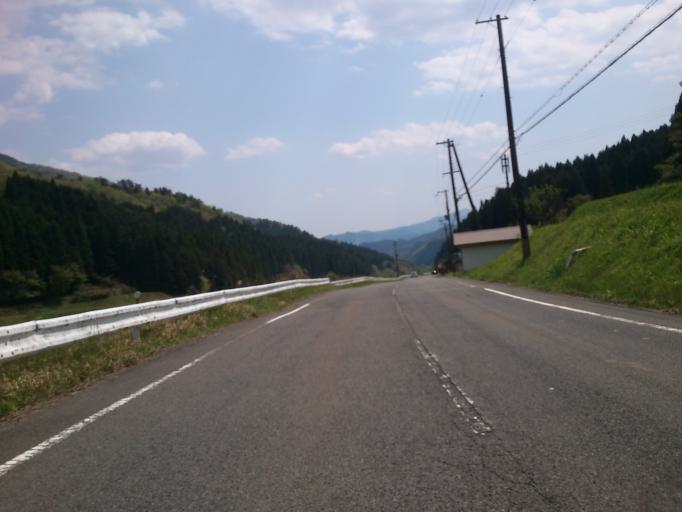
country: JP
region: Hyogo
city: Toyooka
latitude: 35.3893
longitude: 134.9406
